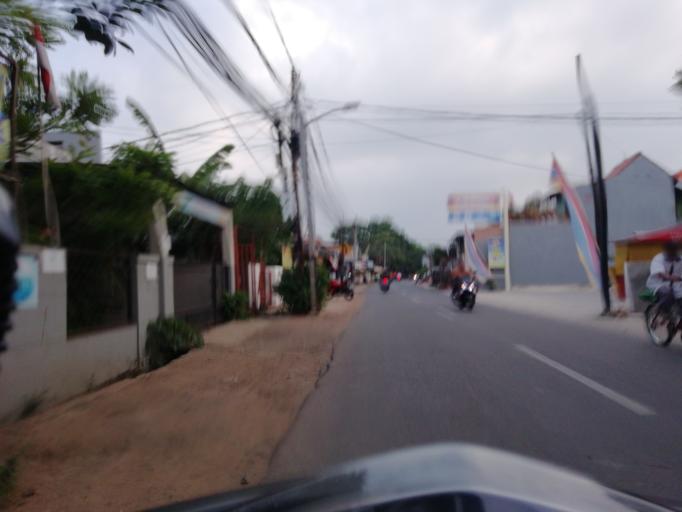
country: ID
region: West Java
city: Depok
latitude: -6.3411
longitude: 106.8276
